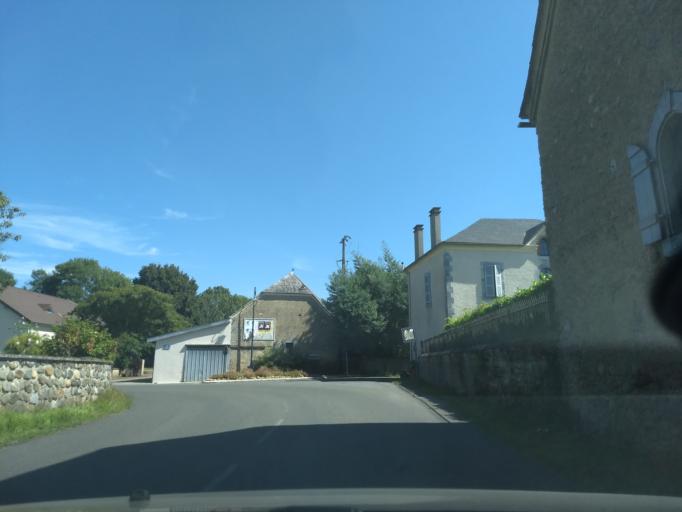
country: FR
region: Aquitaine
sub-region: Departement des Pyrenees-Atlantiques
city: Soumoulou
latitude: 43.2745
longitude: -0.1823
